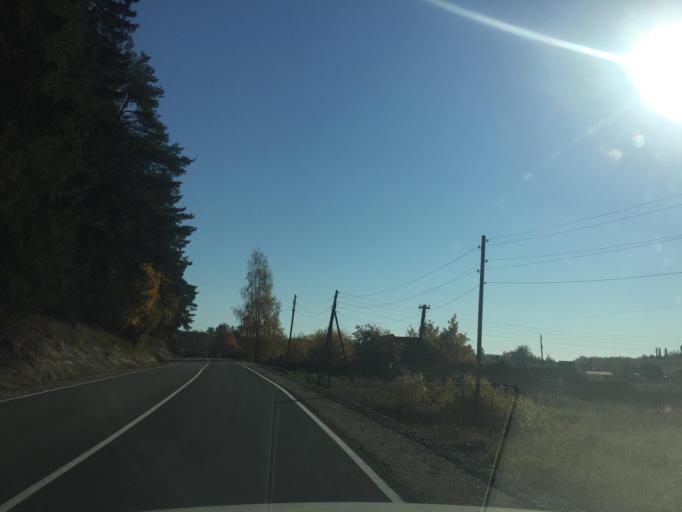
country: RU
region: Leningrad
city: Kuznechnoye
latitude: 61.3031
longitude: 29.8830
